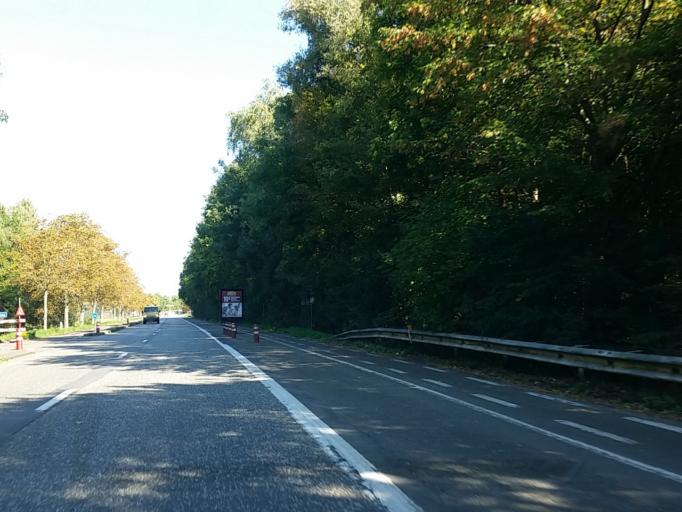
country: BE
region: Flanders
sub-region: Provincie Vlaams-Brabant
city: Machelen
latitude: 50.9263
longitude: 4.4653
